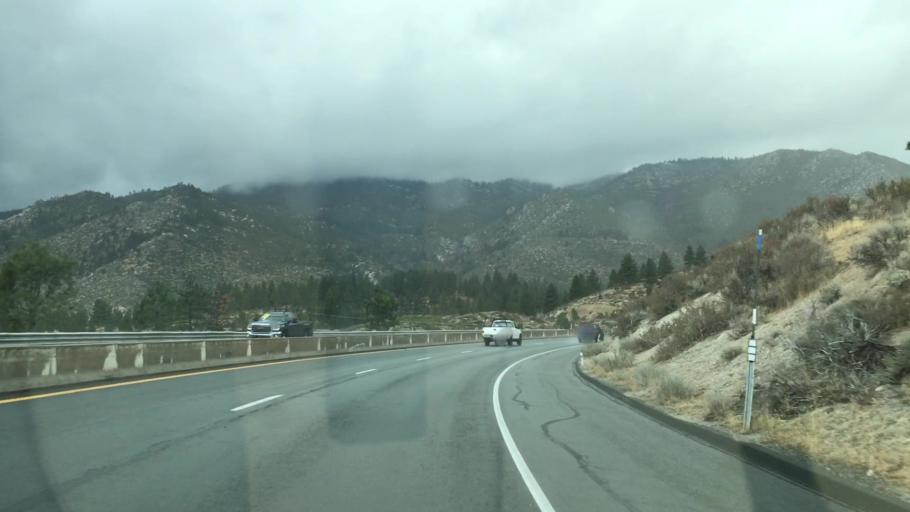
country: US
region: Nevada
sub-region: Douglas County
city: Indian Hills
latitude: 39.1204
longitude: -119.8230
